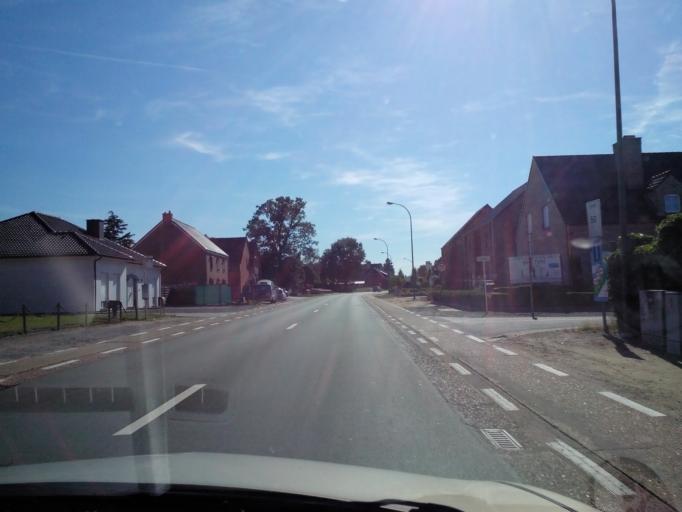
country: BE
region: Flanders
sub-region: Provincie Limburg
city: Opglabbeek
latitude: 51.0407
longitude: 5.5705
